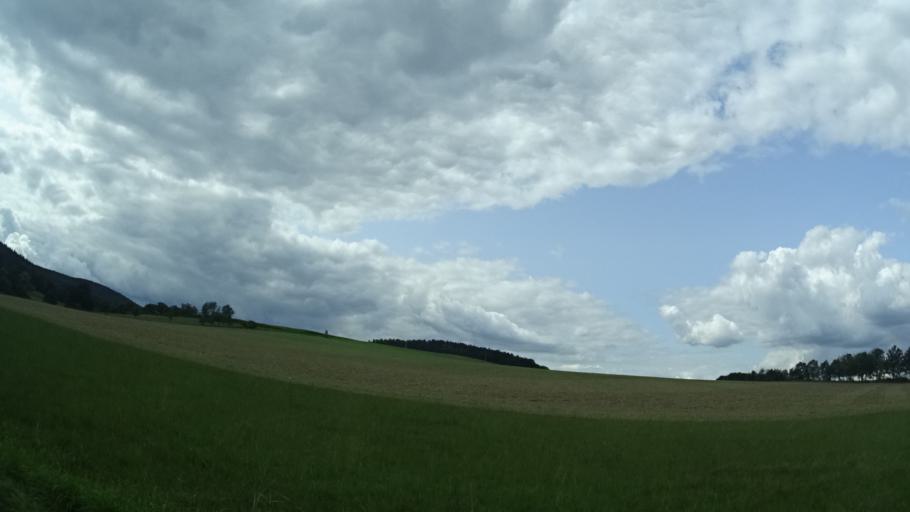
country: DE
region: Thuringia
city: Unterwellenborn
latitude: 50.7175
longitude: 11.4178
